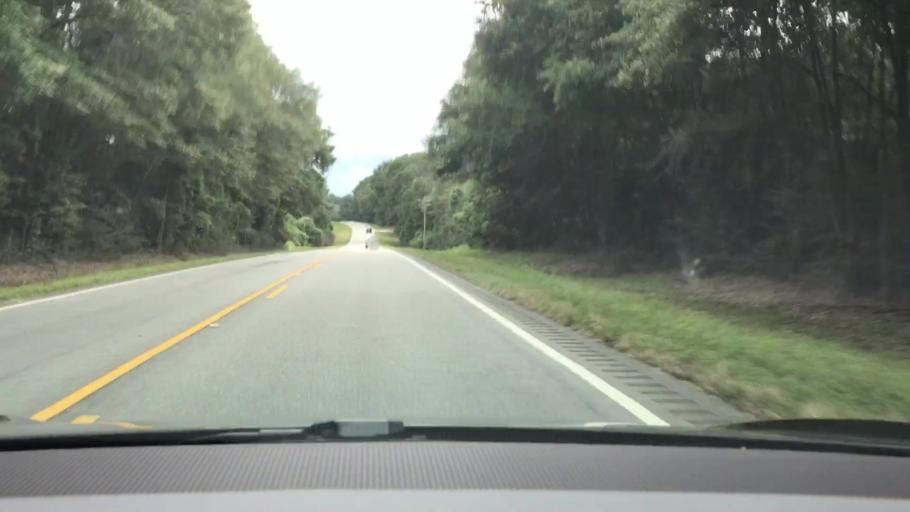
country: US
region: Alabama
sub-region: Coffee County
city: Elba
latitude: 31.5226
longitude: -86.0395
